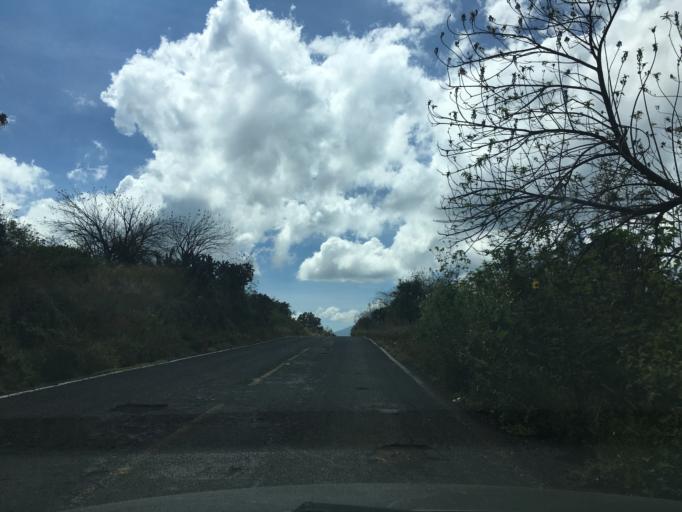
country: MX
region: Michoacan
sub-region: Morelia
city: Cuto de la Esperanza
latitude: 19.7601
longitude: -101.3716
